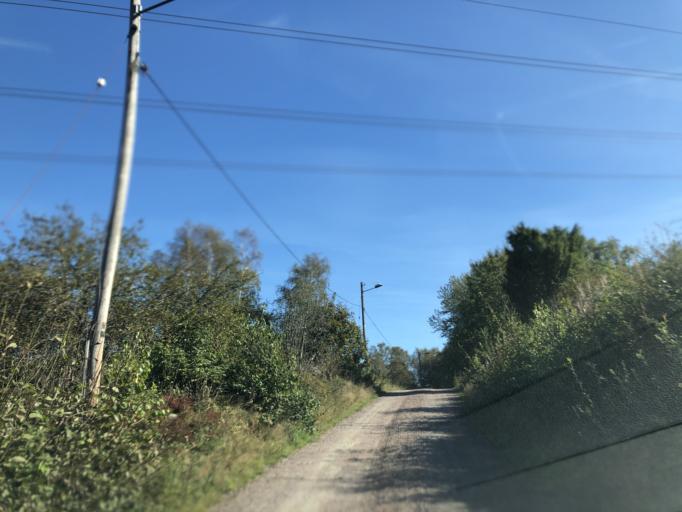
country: SE
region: Vaestra Goetaland
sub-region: Goteborg
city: Majorna
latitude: 57.7651
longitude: 11.9208
